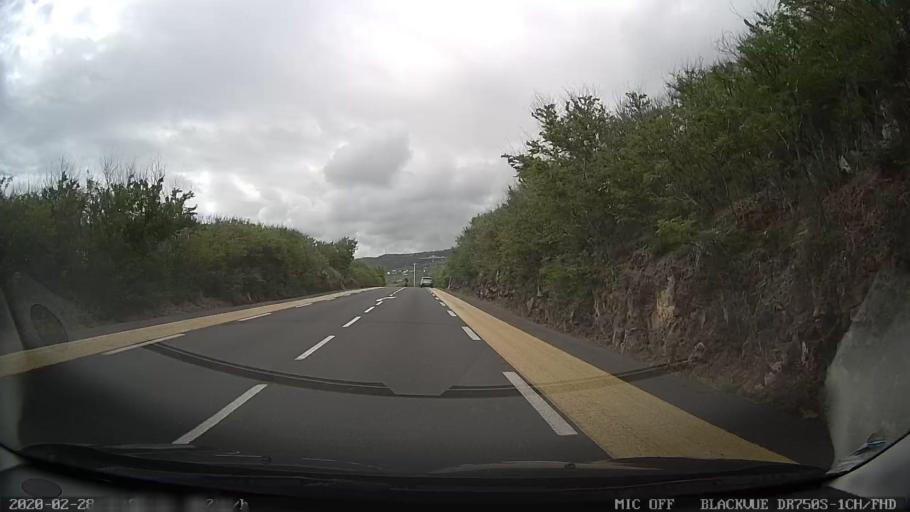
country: RE
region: Reunion
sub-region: Reunion
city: Saint-Leu
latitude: -21.1341
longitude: 55.2719
